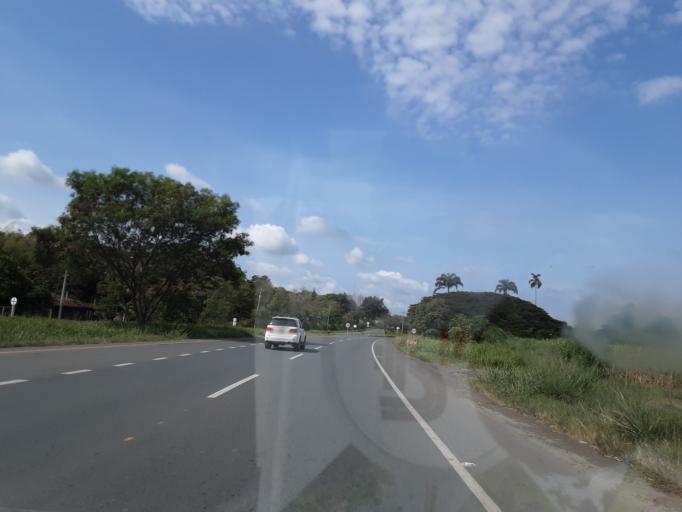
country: CO
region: Valle del Cauca
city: Guacari
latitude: 3.7983
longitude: -76.3112
